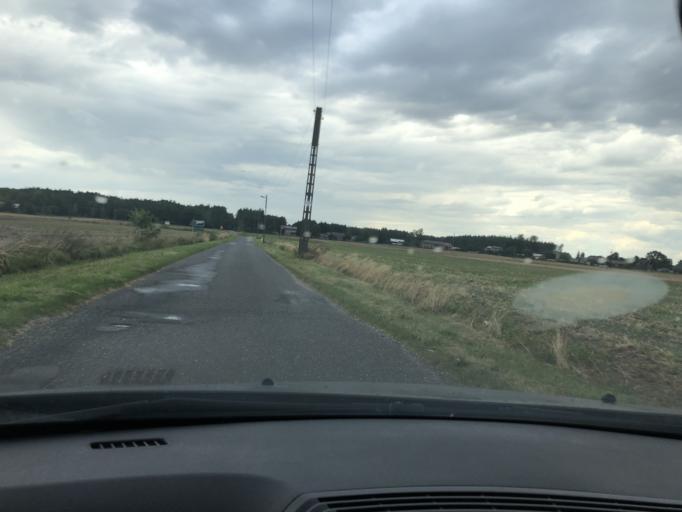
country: PL
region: Lodz Voivodeship
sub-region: Powiat wieruszowski
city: Czastary
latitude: 51.2395
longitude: 18.3001
